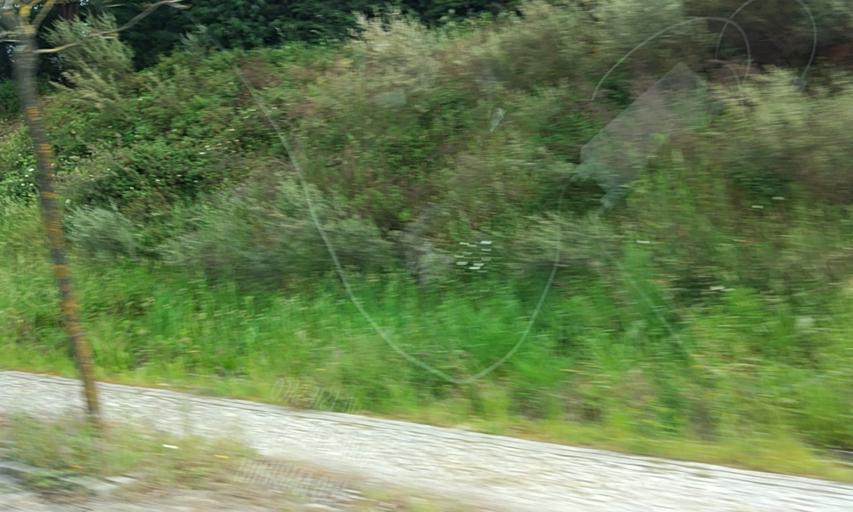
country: PT
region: Evora
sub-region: Evora
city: Evora
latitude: 38.5675
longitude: -7.9376
